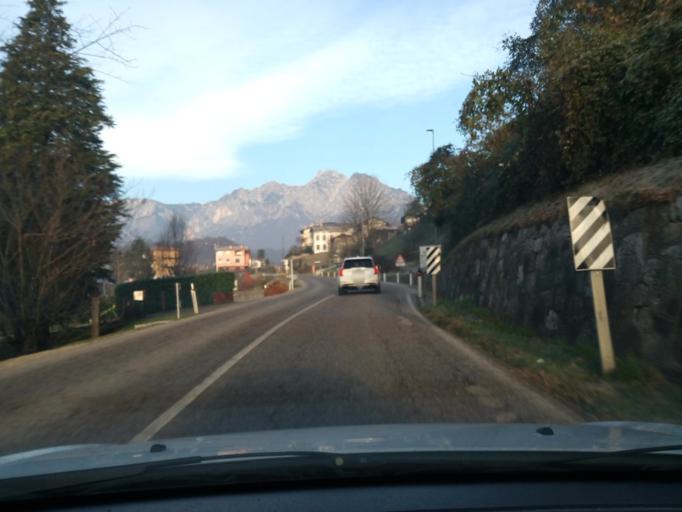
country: IT
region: Veneto
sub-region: Provincia di Vicenza
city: Valli del Pasubio
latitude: 45.7355
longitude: 11.2697
